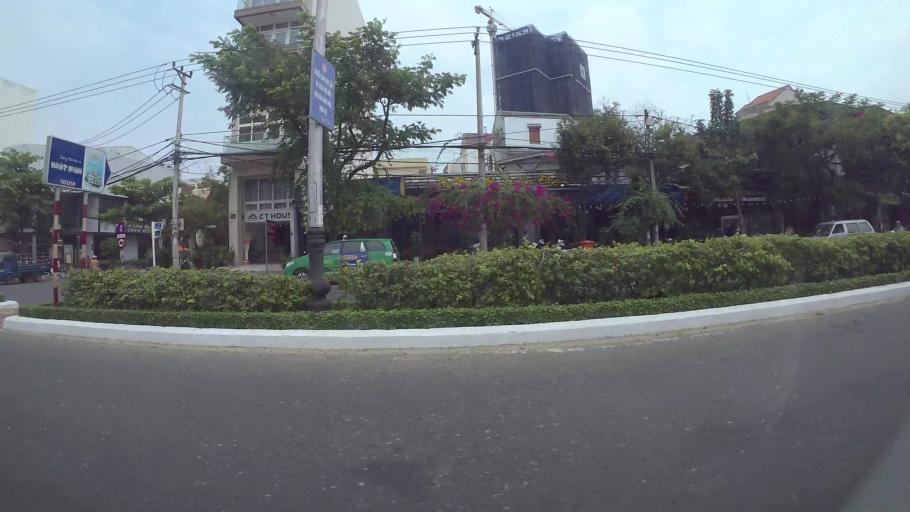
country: VN
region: Da Nang
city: Da Nang
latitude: 16.0852
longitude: 108.2198
